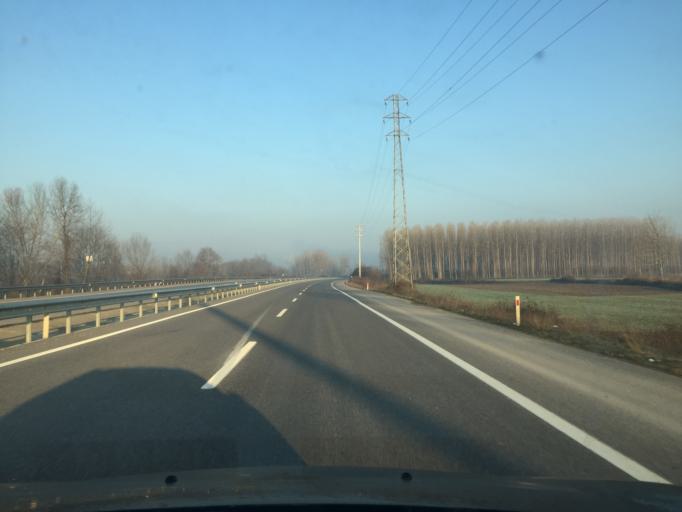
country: TR
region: Sakarya
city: Akyazi
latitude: 40.6536
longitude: 30.6008
